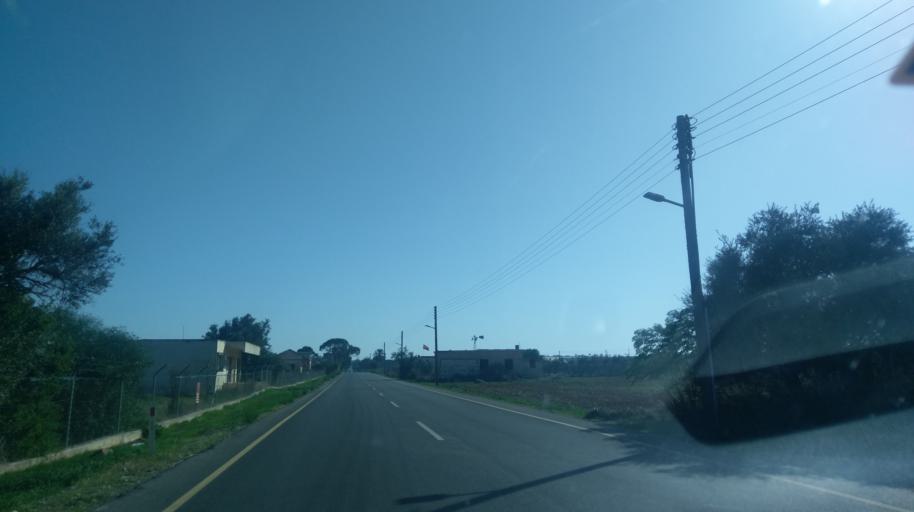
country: CY
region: Ammochostos
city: Deryneia
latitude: 35.0919
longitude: 33.9529
